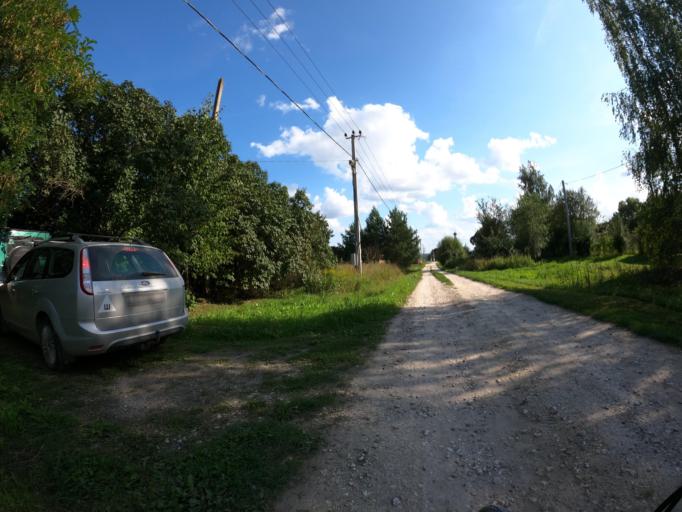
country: RU
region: Moskovskaya
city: Troitskoye
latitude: 55.2152
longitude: 38.4878
